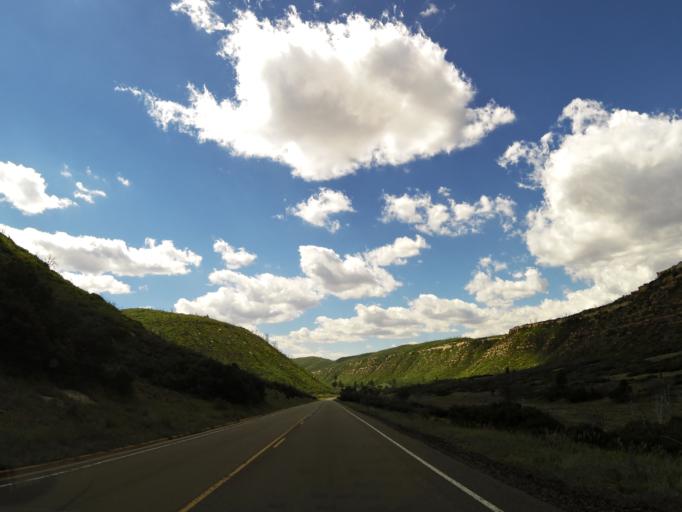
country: US
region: Colorado
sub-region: Montezuma County
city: Mancos
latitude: 37.2919
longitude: -108.4133
